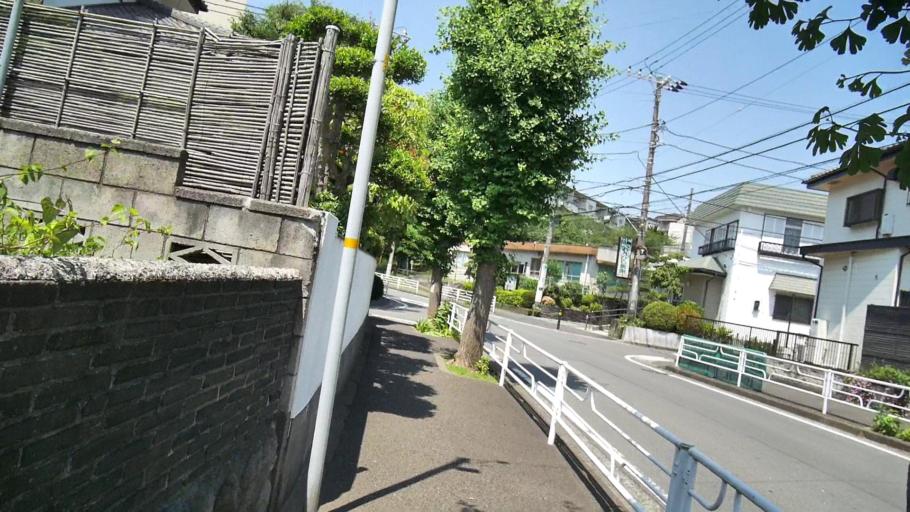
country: JP
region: Kanagawa
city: Fujisawa
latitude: 35.3983
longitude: 139.5187
